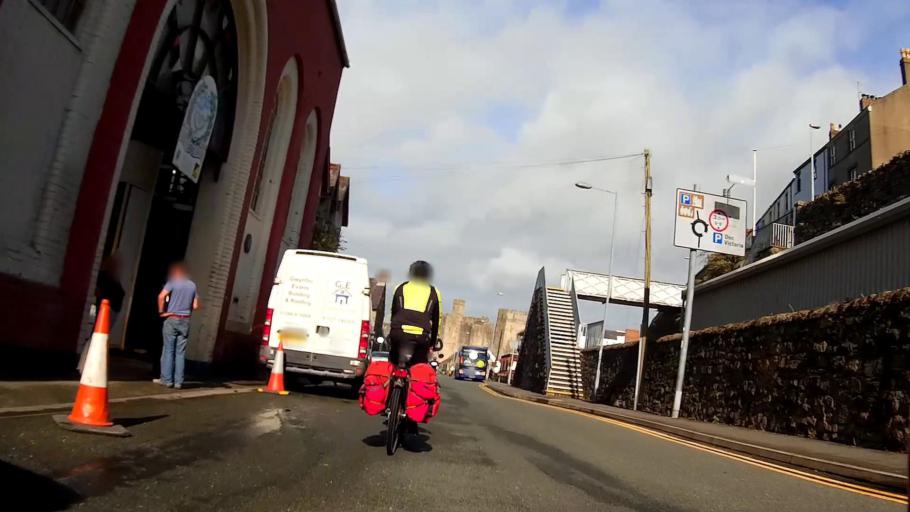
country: GB
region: Wales
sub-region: Gwynedd
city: Caernarfon
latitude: 53.1375
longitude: -4.2722
